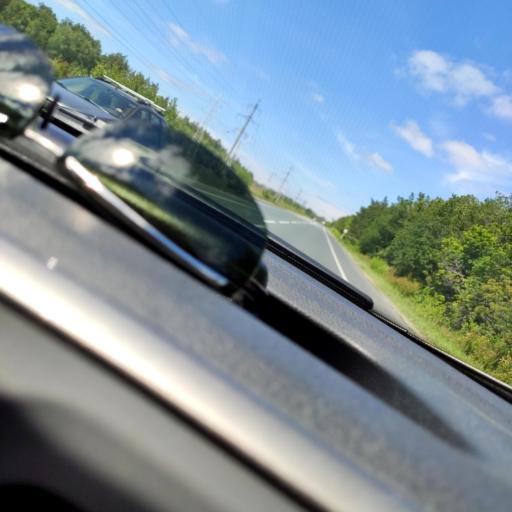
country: RU
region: Samara
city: Bogatyr'
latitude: 53.5057
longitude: 49.9403
